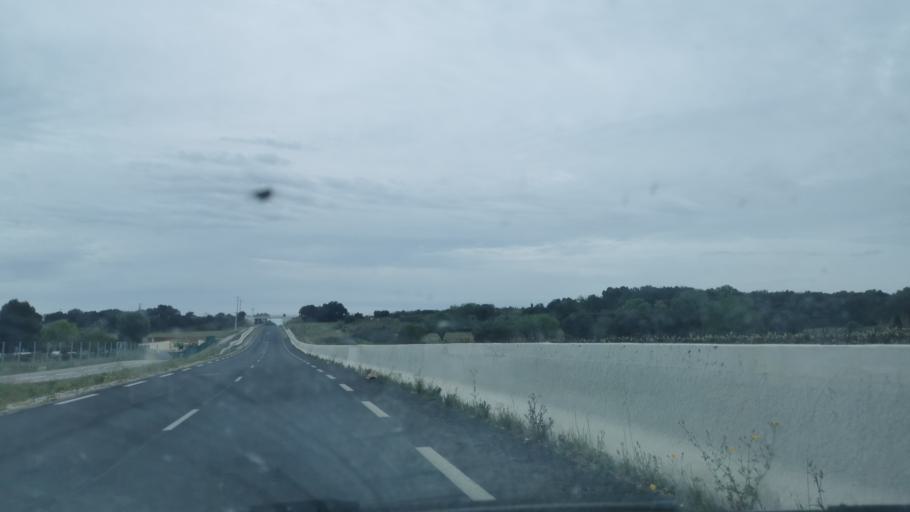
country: FR
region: Languedoc-Roussillon
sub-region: Departement de l'Herault
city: Montbazin
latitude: 43.5235
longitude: 3.6863
